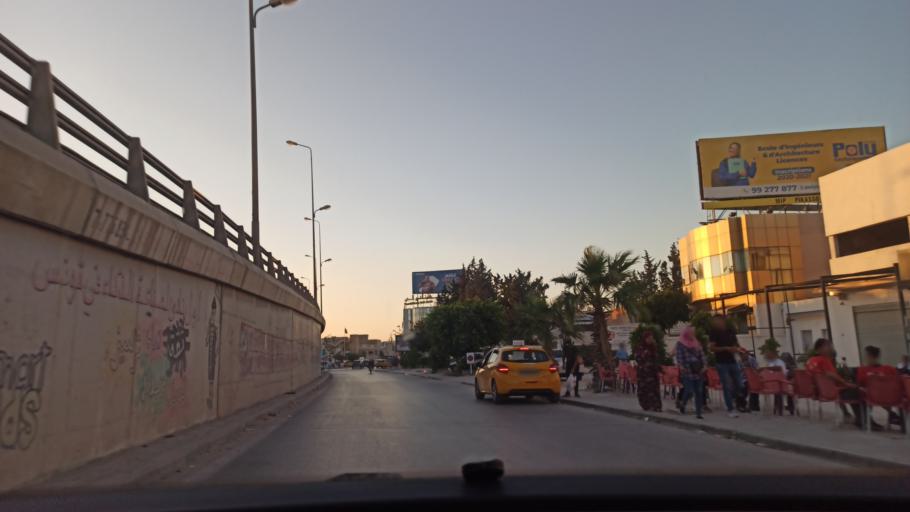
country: TN
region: Ariana
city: Ariana
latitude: 36.8636
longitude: 10.2013
